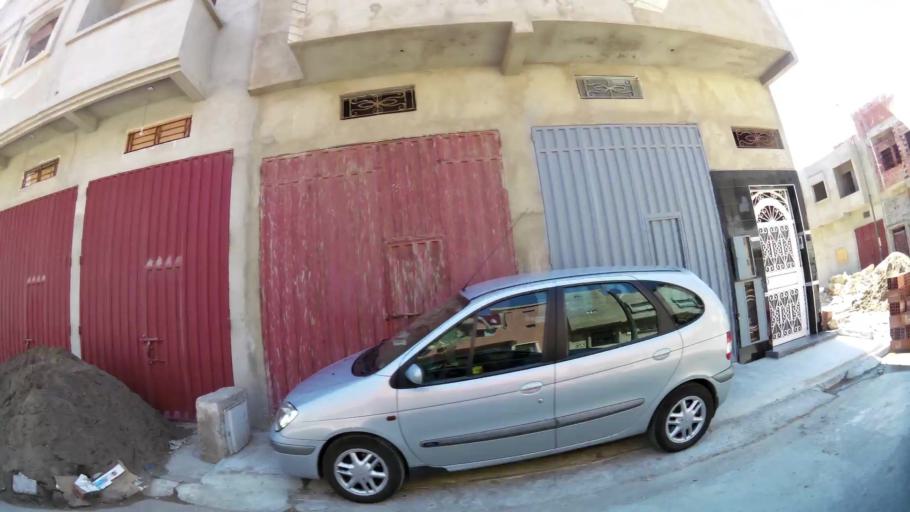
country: MA
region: Gharb-Chrarda-Beni Hssen
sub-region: Kenitra Province
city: Kenitra
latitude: 34.2298
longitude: -6.5511
